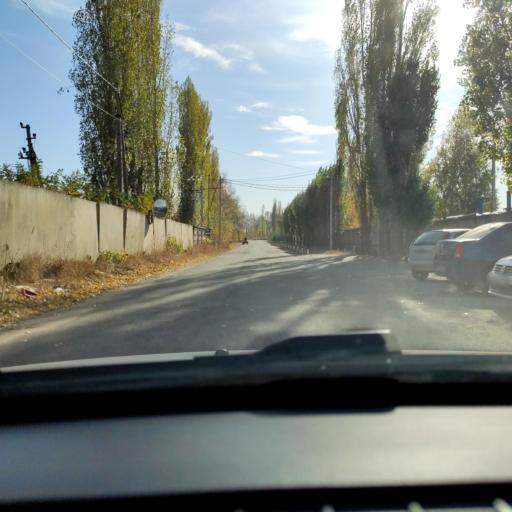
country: RU
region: Voronezj
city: Podgornoye
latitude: 51.8055
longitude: 39.1997
